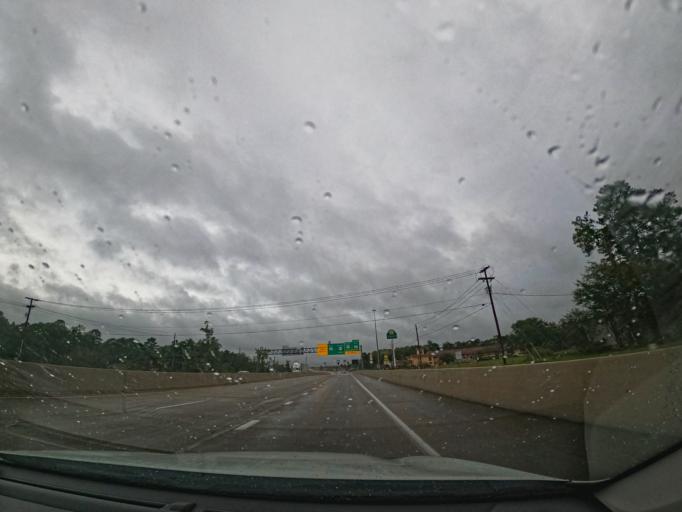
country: US
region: Texas
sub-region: Angelina County
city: Lufkin
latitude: 31.3039
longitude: -94.7265
